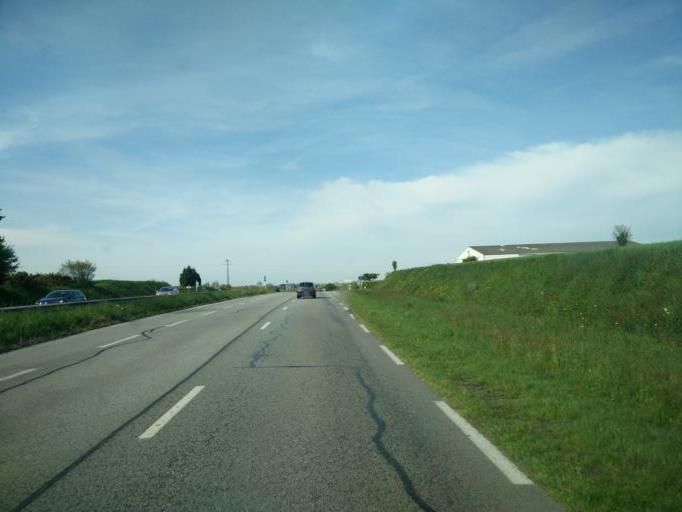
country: FR
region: Lower Normandy
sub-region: Departement de la Manche
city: Le Val-Saint-Pere
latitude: 48.5956
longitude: -1.4088
